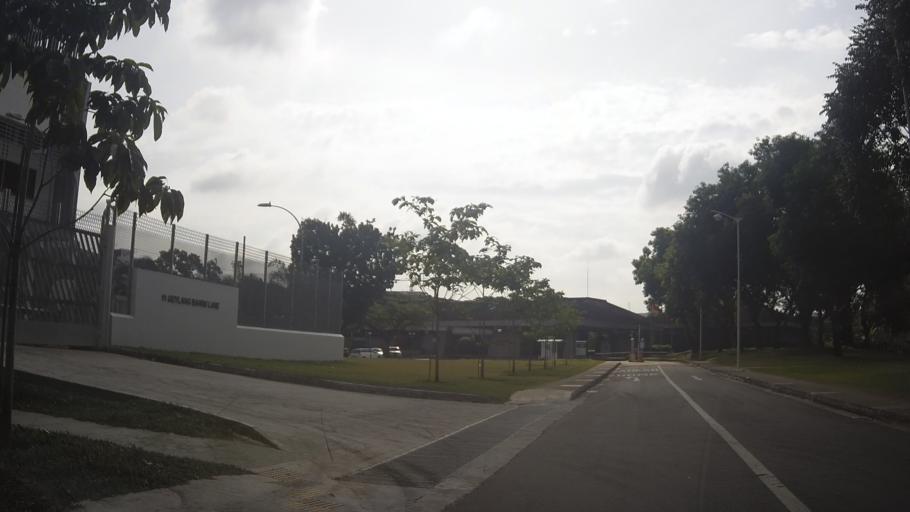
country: SG
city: Singapore
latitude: 1.3235
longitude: 103.8711
